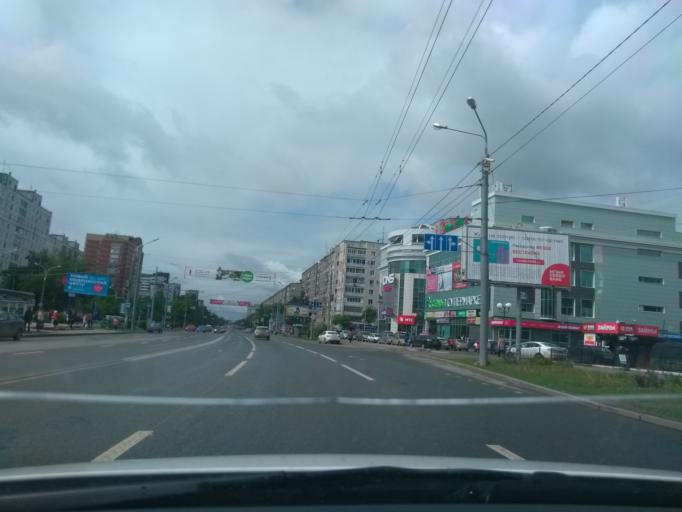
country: RU
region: Perm
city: Kondratovo
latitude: 57.9987
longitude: 56.1570
